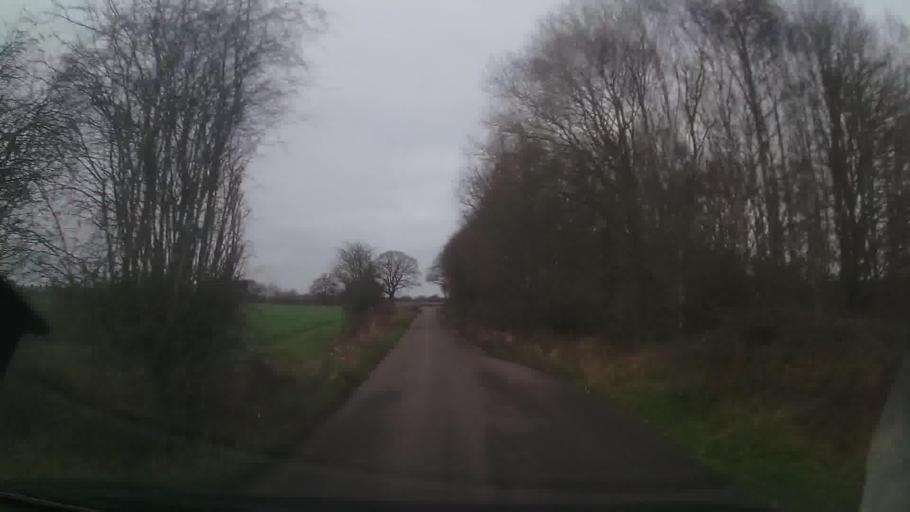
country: GB
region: England
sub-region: Shropshire
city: Petton
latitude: 52.8385
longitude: -2.7860
